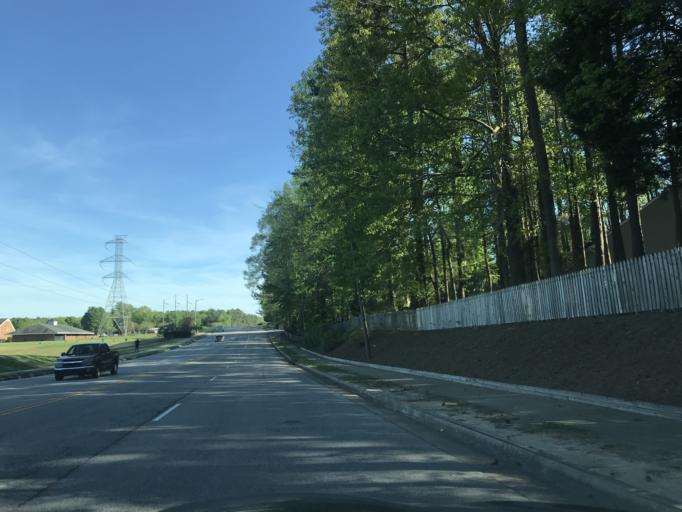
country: US
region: North Carolina
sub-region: Wake County
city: Knightdale
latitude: 35.8073
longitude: -78.5562
